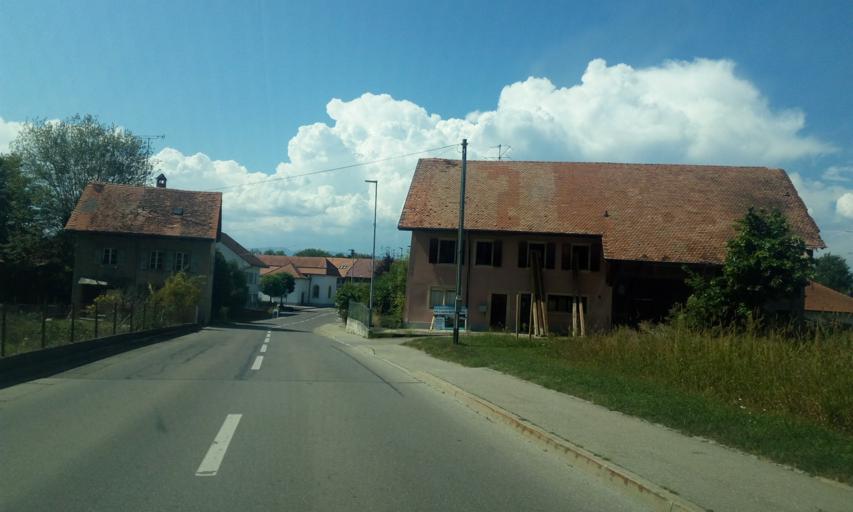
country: CH
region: Fribourg
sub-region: Broye District
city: Domdidier
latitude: 46.9130
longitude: 6.9694
